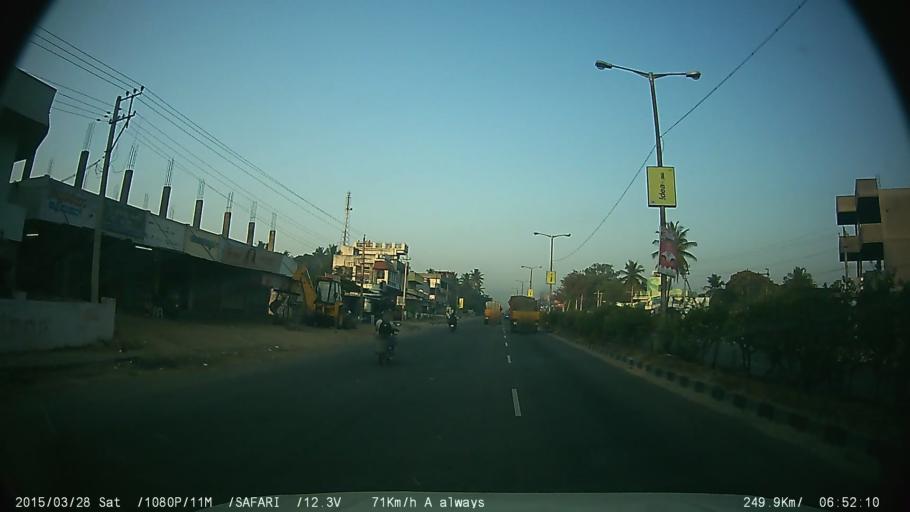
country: IN
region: Karnataka
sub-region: Mandya
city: Maddur
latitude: 12.5926
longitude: 77.0494
